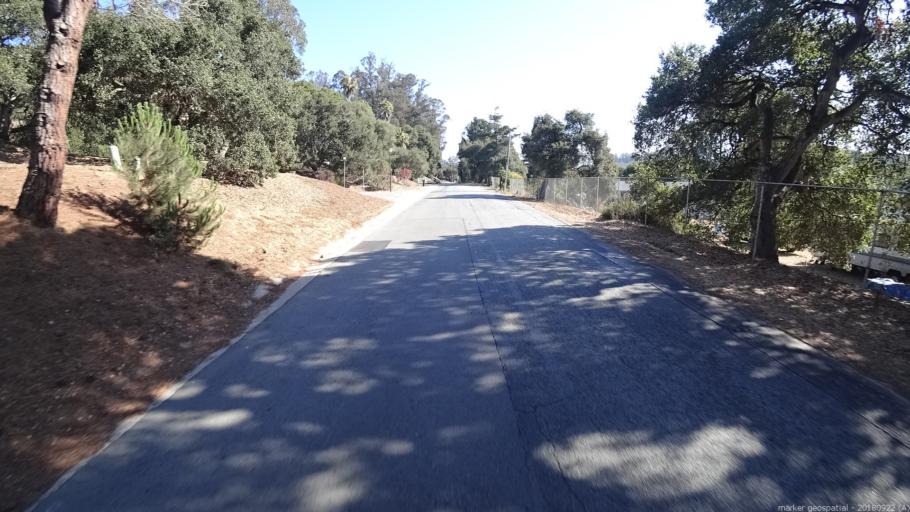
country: US
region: California
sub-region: Monterey County
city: Prunedale
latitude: 36.8117
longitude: -121.6450
